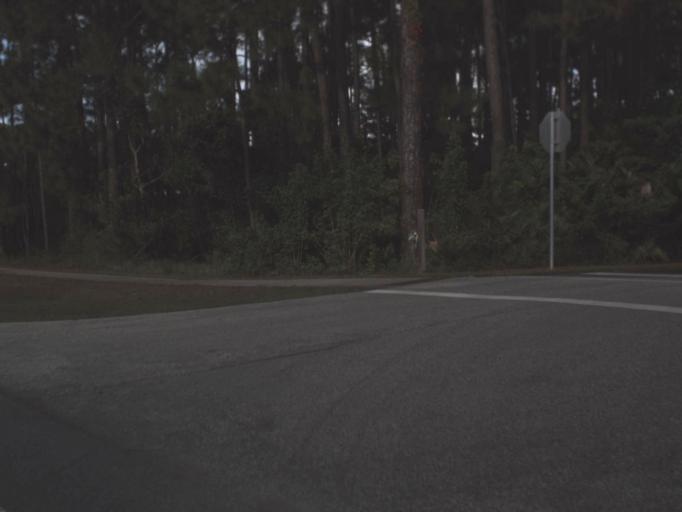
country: US
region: Florida
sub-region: Volusia County
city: Daytona Beach
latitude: 29.1920
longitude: -81.0830
